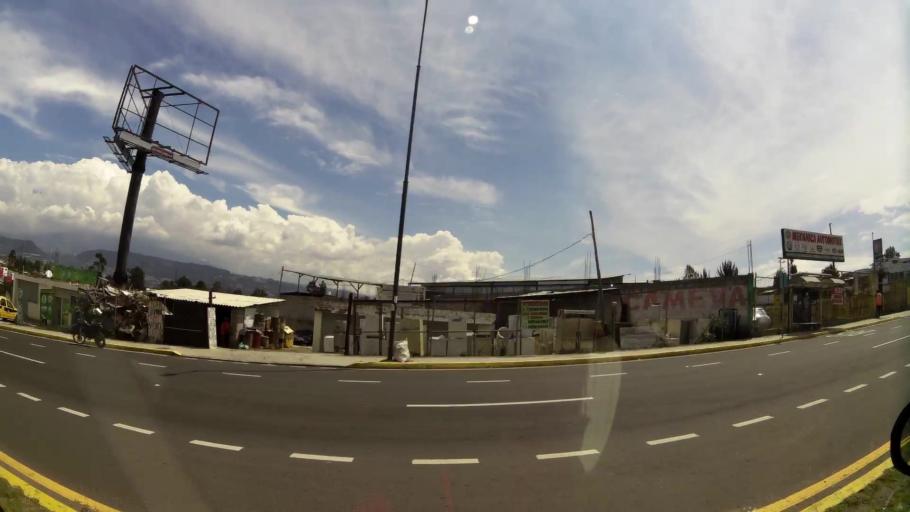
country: EC
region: Pichincha
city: Quito
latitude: -0.2065
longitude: -78.3806
